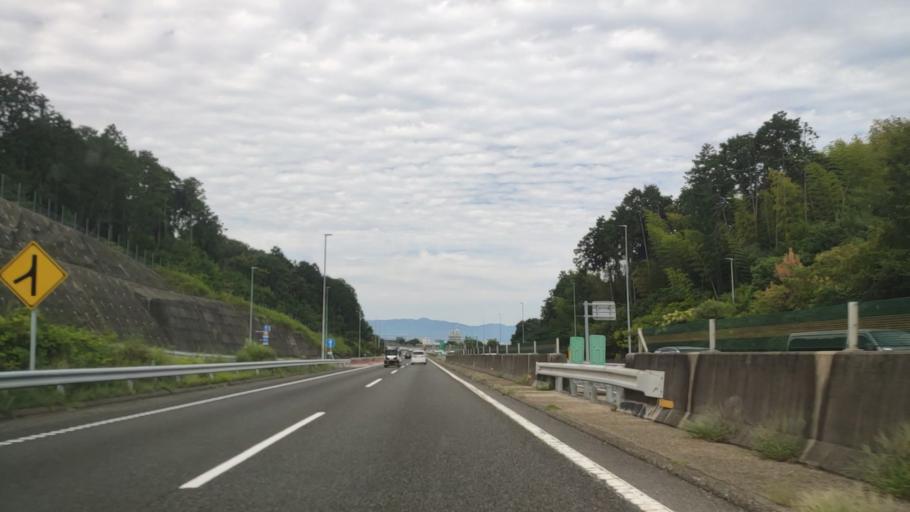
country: JP
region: Shiga Prefecture
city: Kusatsu
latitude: 35.0199
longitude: 136.0192
